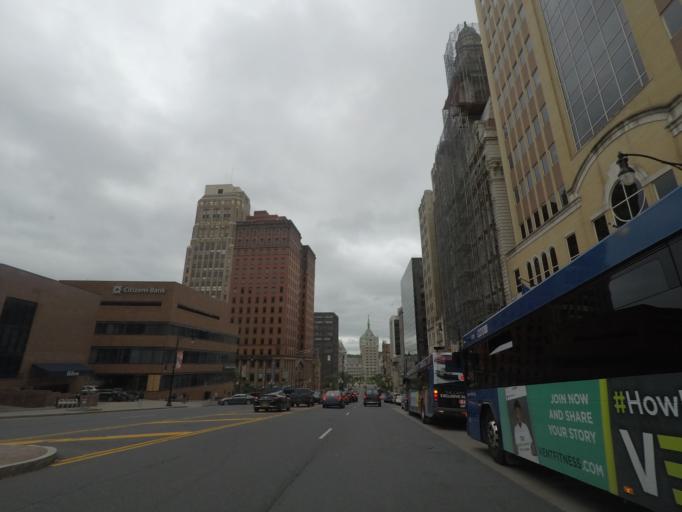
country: US
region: New York
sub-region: Albany County
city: Albany
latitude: 42.6503
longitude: -73.7539
